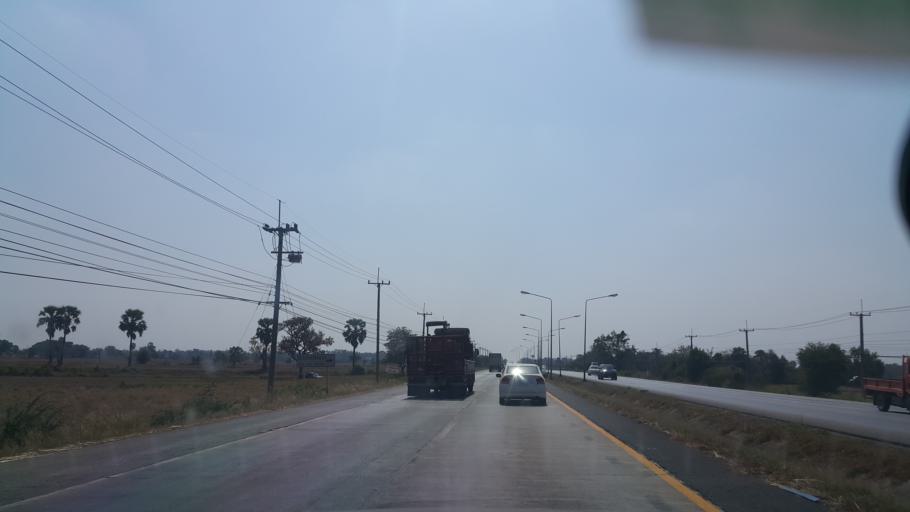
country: TH
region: Nakhon Ratchasima
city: Sida
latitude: 15.5151
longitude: 102.5376
